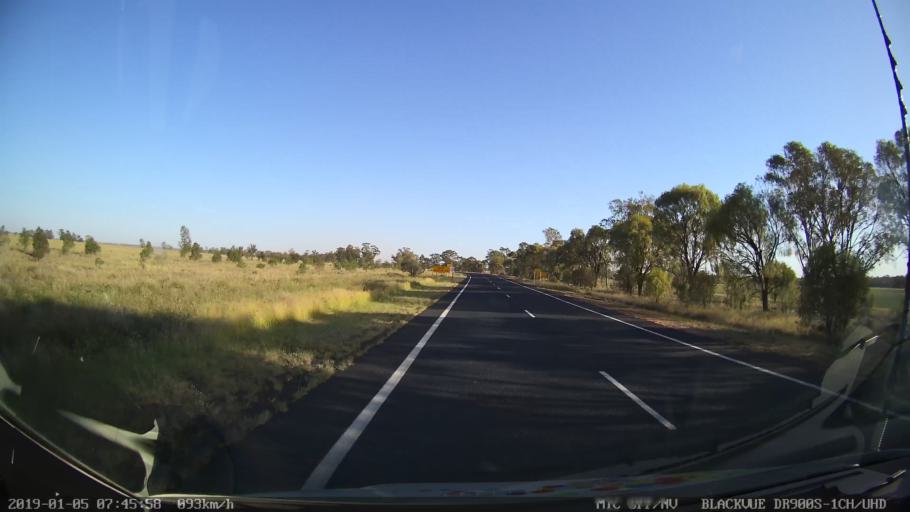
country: AU
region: New South Wales
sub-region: Gilgandra
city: Gilgandra
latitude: -31.8510
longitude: 148.6442
